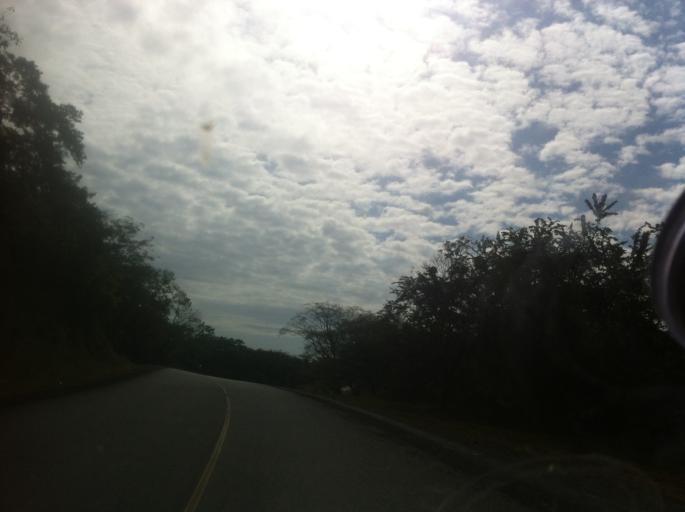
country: NI
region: Rio San Juan
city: San Miguelito
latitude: 11.3830
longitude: -84.7906
